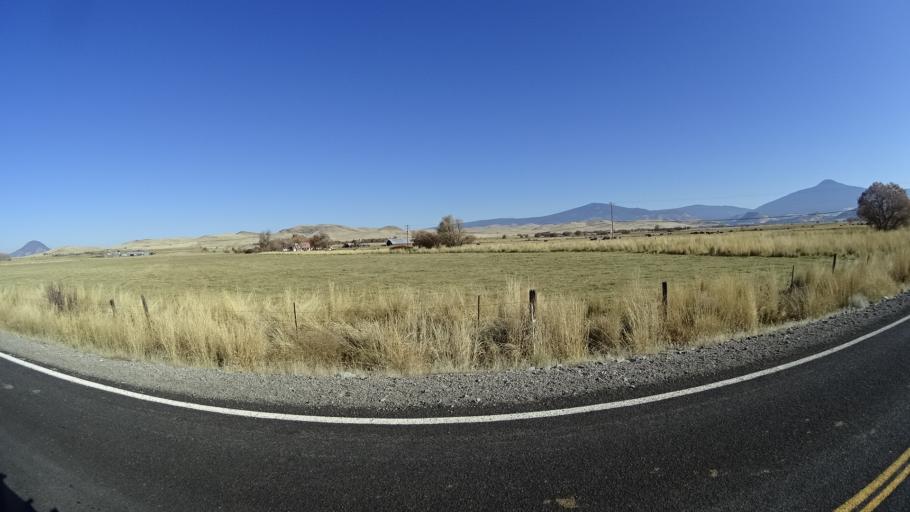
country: US
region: California
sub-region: Siskiyou County
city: Montague
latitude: 41.7126
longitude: -122.4388
